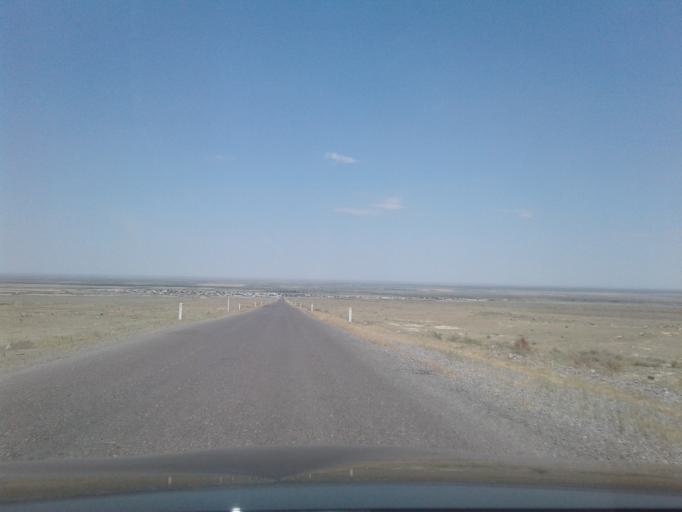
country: TM
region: Ahal
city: Baharly
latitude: 38.5161
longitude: 57.1353
